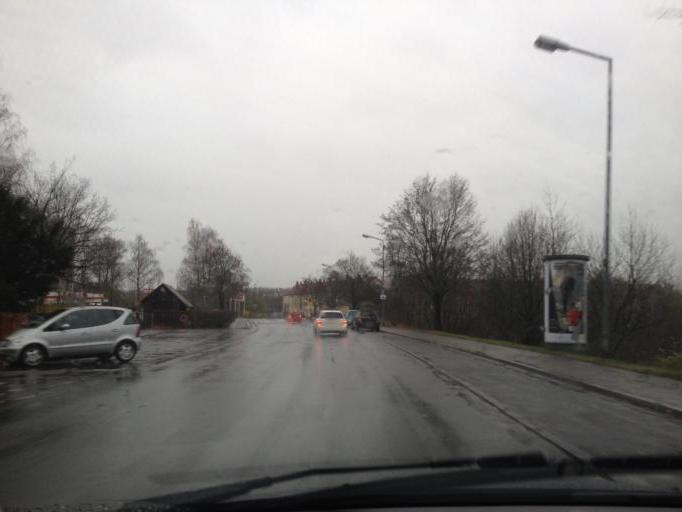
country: DE
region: Bavaria
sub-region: Regierungsbezirk Mittelfranken
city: Lauf an der Pegnitz
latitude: 49.5039
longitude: 11.2758
